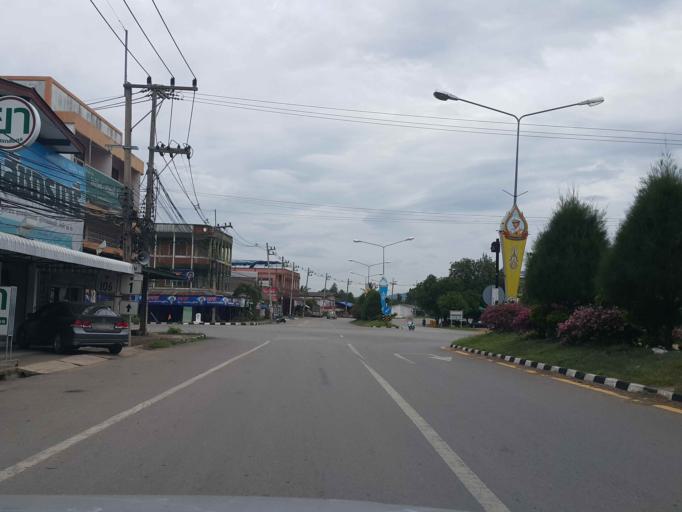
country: TH
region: Lampang
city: Thoen
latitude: 17.6400
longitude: 99.2356
